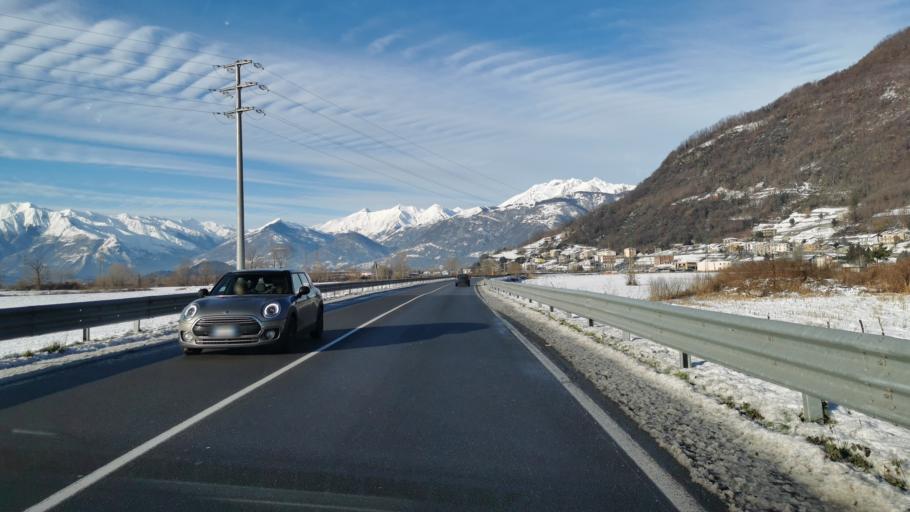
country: IT
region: Lombardy
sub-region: Provincia di Sondrio
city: Delebio
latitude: 46.1510
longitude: 9.4510
